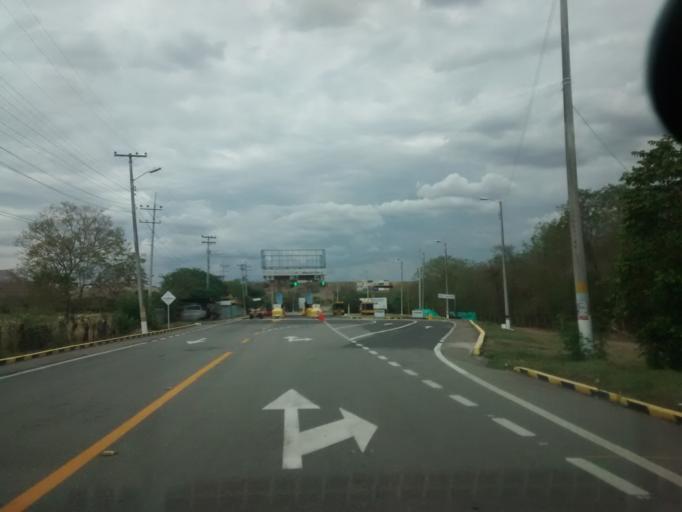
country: CO
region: Cundinamarca
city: Agua de Dios
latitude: 4.4027
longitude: -74.7323
